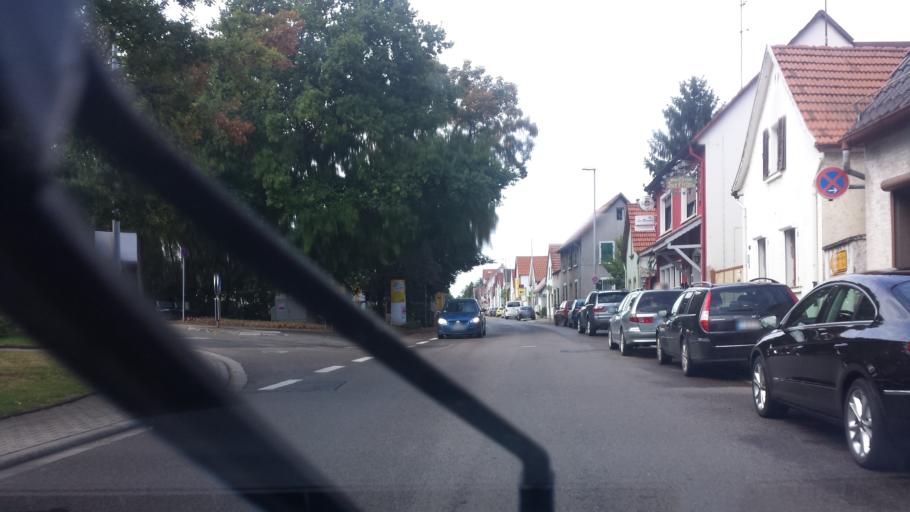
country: DE
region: Rheinland-Pfalz
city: Osthofen
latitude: 49.7032
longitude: 8.3157
